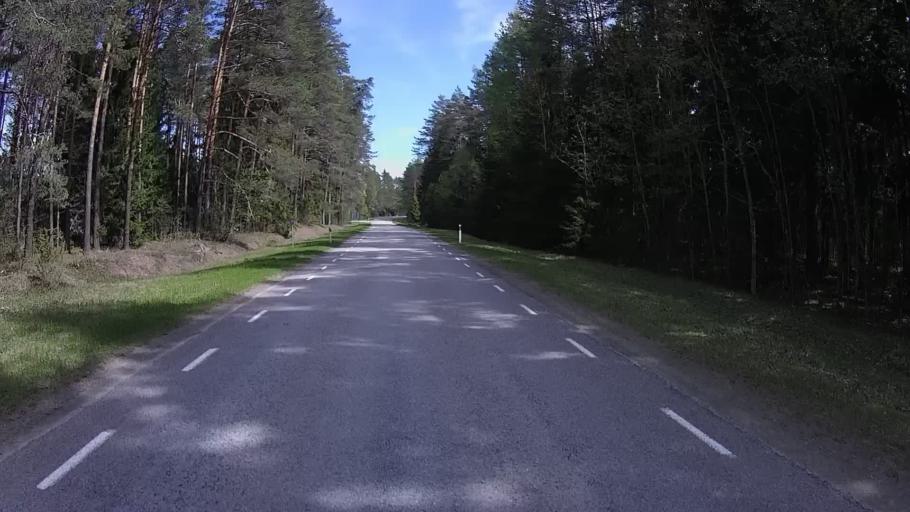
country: LV
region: Apes Novads
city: Ape
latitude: 57.6049
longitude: 26.4732
